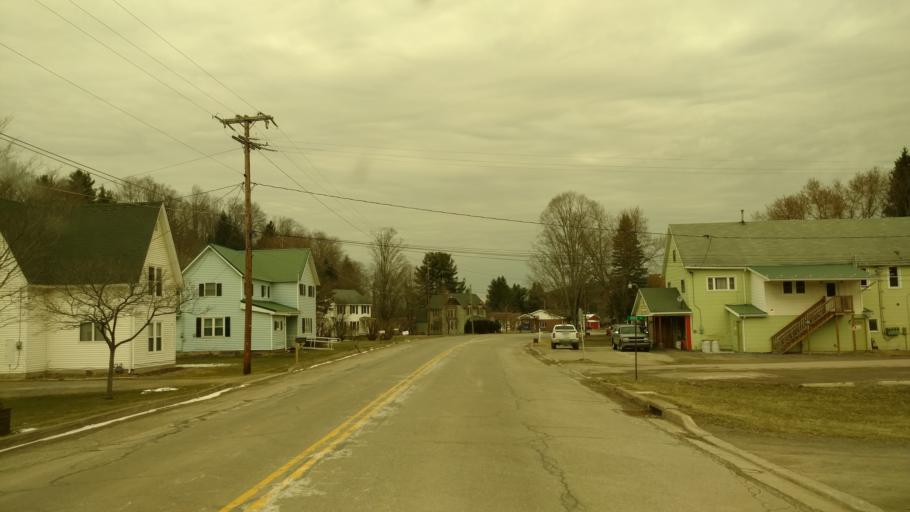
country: US
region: New York
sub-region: Allegany County
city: Wellsville
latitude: 41.9921
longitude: -77.8705
